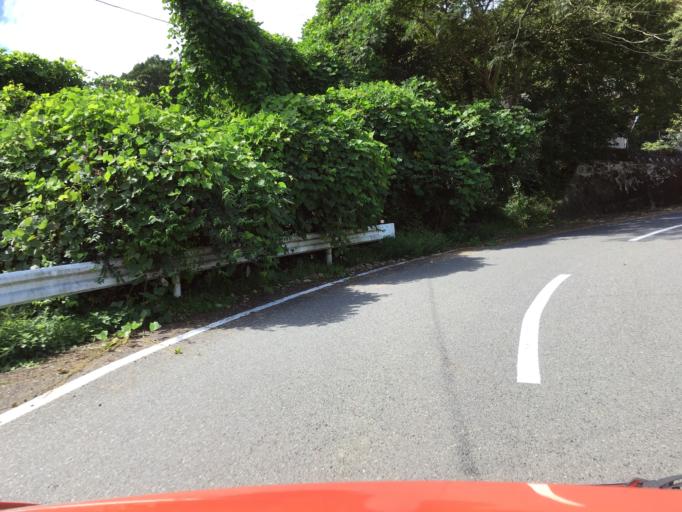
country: JP
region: Okayama
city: Tsuyama
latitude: 34.8996
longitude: 134.1307
